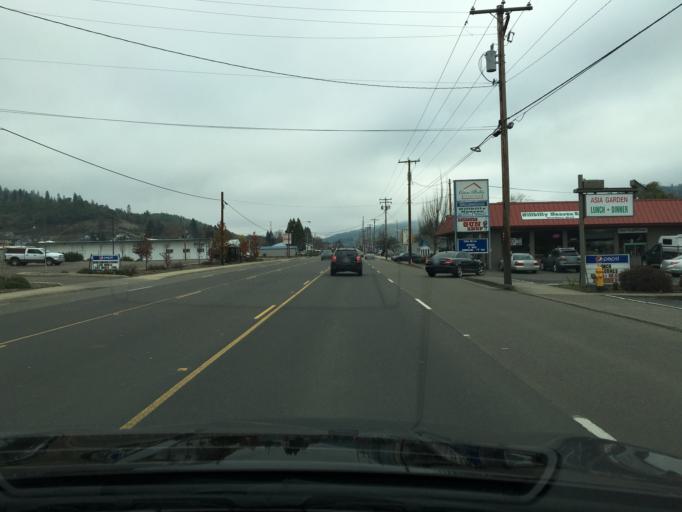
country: US
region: Oregon
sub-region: Douglas County
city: Roseburg
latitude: 43.2130
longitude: -123.3275
